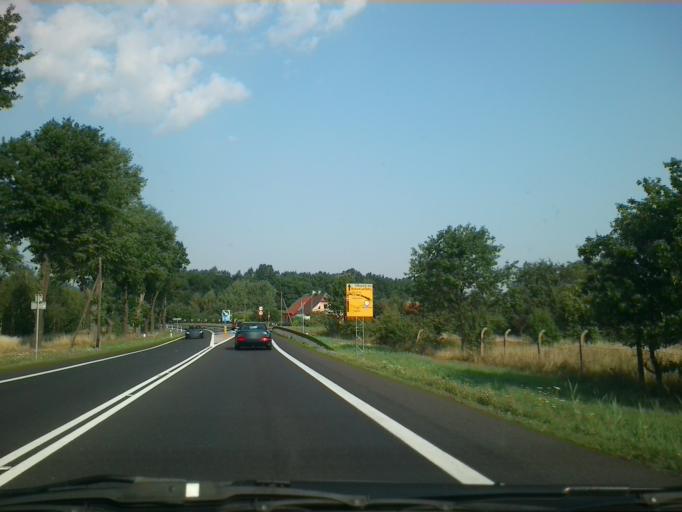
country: PL
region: Lubusz
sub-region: Powiat nowosolski
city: Nowe Miasteczko
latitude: 51.6802
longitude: 15.7726
